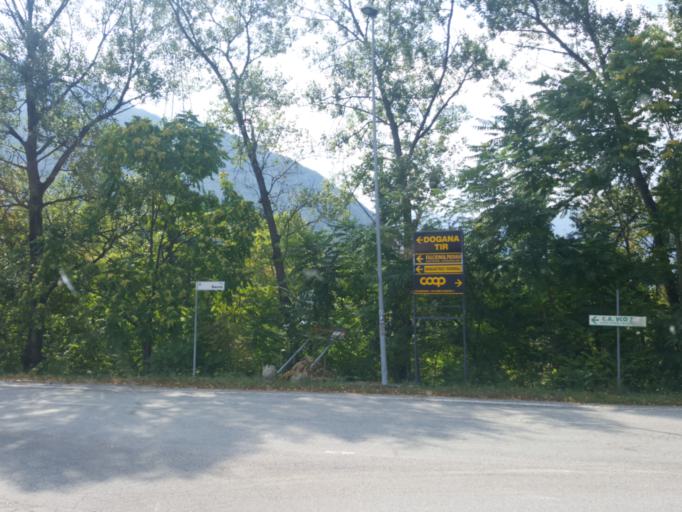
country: IT
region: Piedmont
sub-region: Provincia Verbano-Cusio-Ossola
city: Villadossola
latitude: 46.0709
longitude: 8.2760
